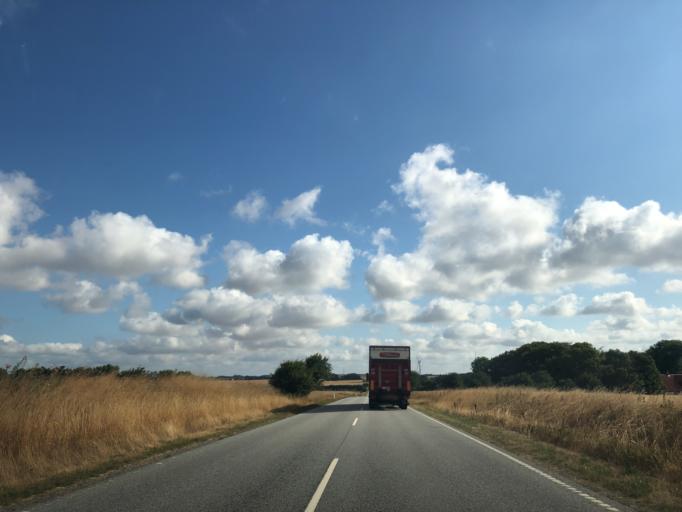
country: DK
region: Central Jutland
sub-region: Skive Kommune
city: Skive
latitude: 56.6615
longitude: 8.9428
